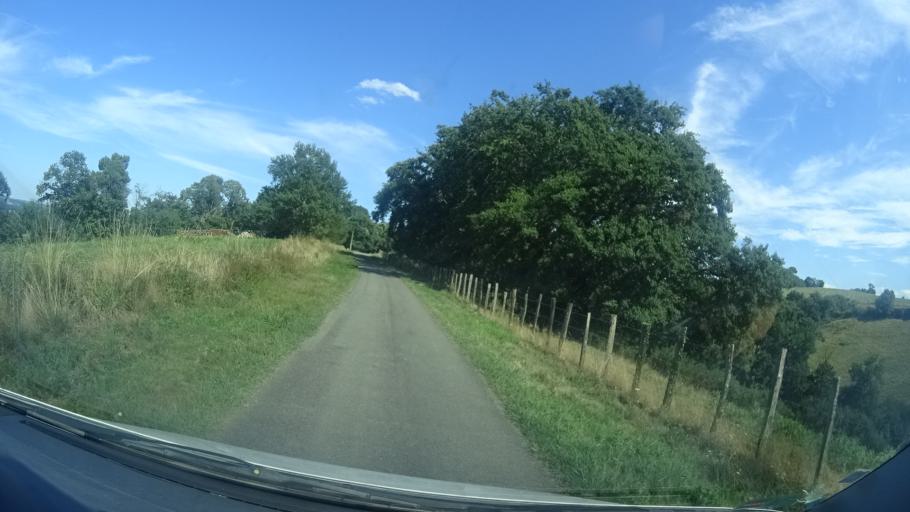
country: FR
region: Aquitaine
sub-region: Departement des Pyrenees-Atlantiques
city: Mont
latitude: 43.4975
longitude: -0.6722
